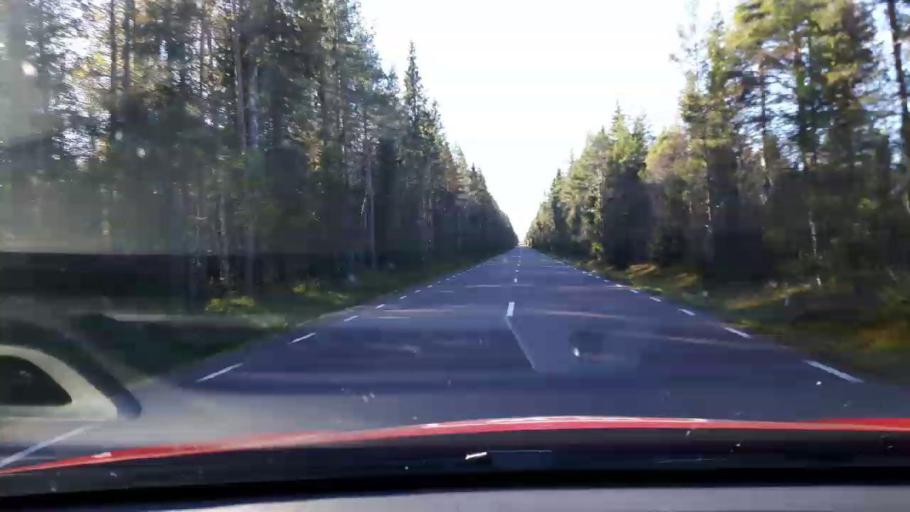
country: SE
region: Jaemtland
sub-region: Stroemsunds Kommun
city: Stroemsund
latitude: 63.8526
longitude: 15.2426
